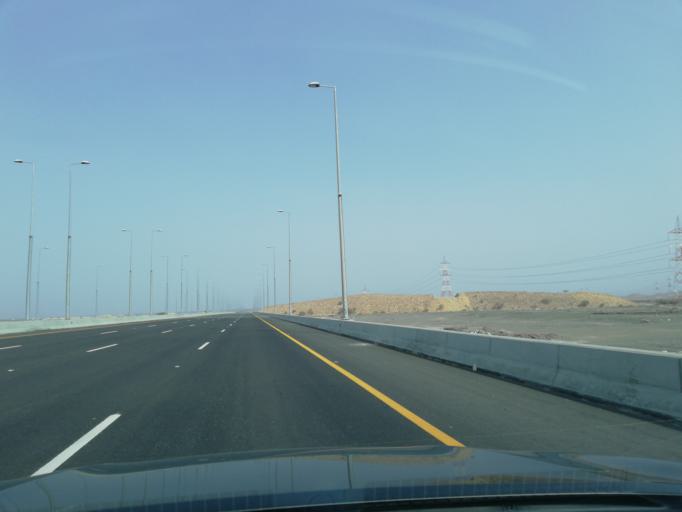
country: OM
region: Al Batinah
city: Al Sohar
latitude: 24.3248
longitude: 56.5673
